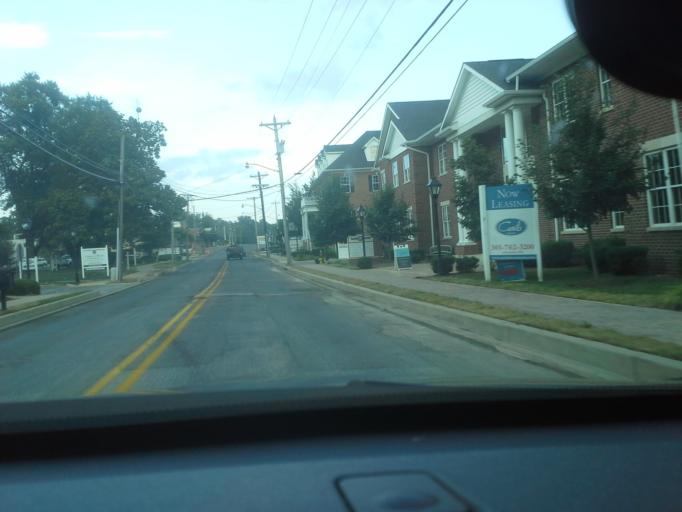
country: US
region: Maryland
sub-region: Calvert County
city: Prince Frederick
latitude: 38.5401
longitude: -76.5846
